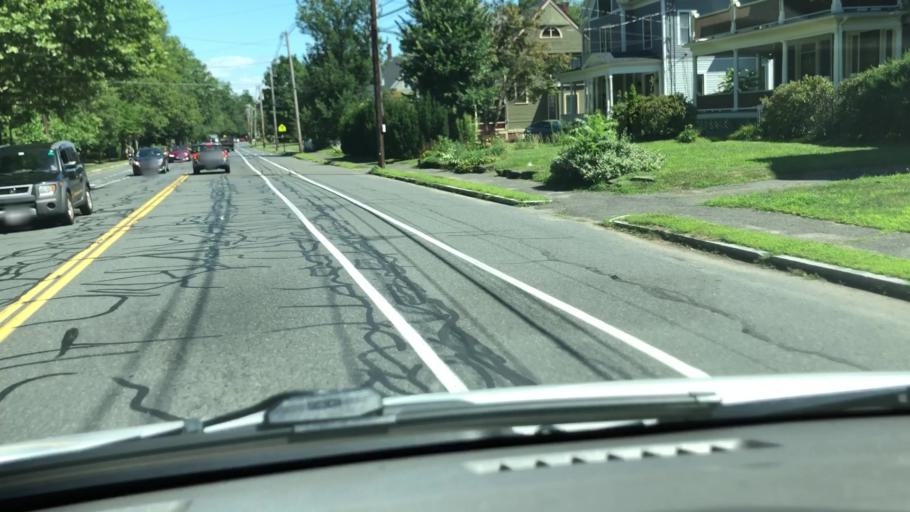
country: US
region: Massachusetts
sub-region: Hampshire County
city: Northampton
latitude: 42.3242
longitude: -72.6482
